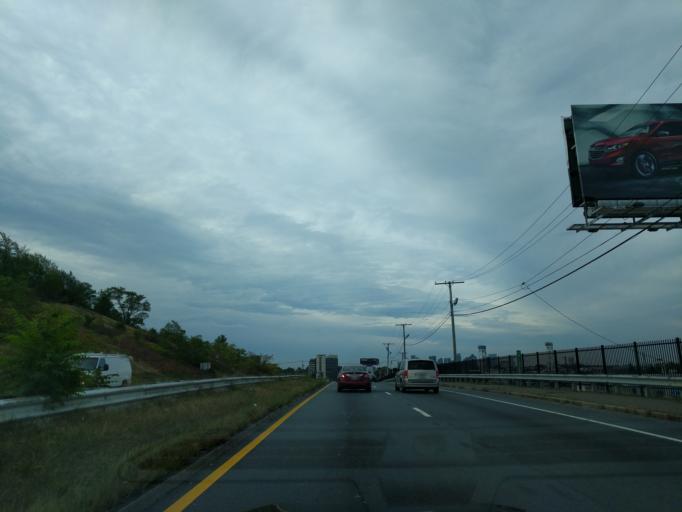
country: US
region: Massachusetts
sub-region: Suffolk County
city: Revere
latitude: 42.3934
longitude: -71.0117
